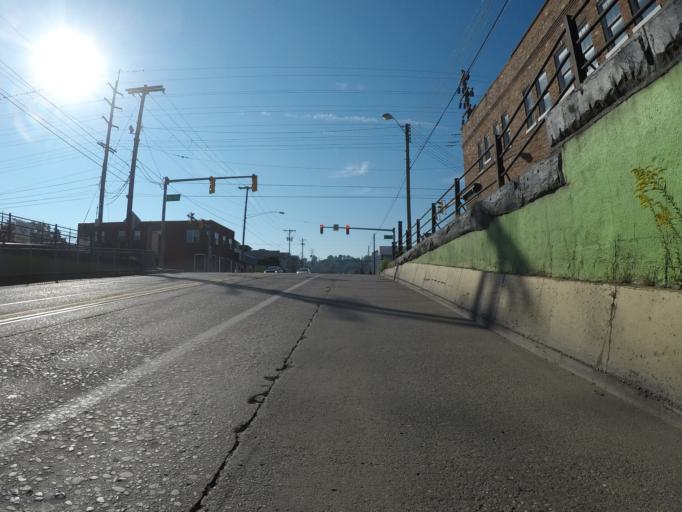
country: US
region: West Virginia
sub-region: Cabell County
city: Huntington
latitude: 38.4151
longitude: -82.4441
